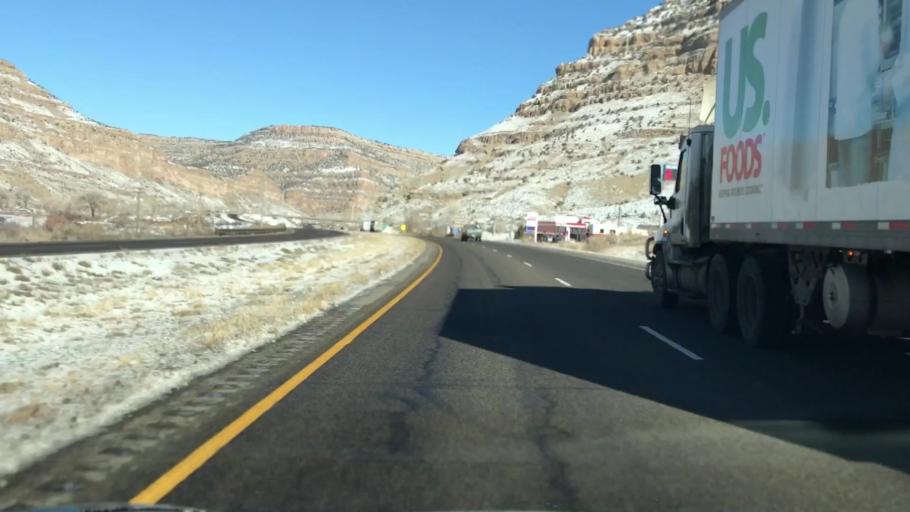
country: US
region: Colorado
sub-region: Mesa County
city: Palisade
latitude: 39.1560
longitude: -108.3008
